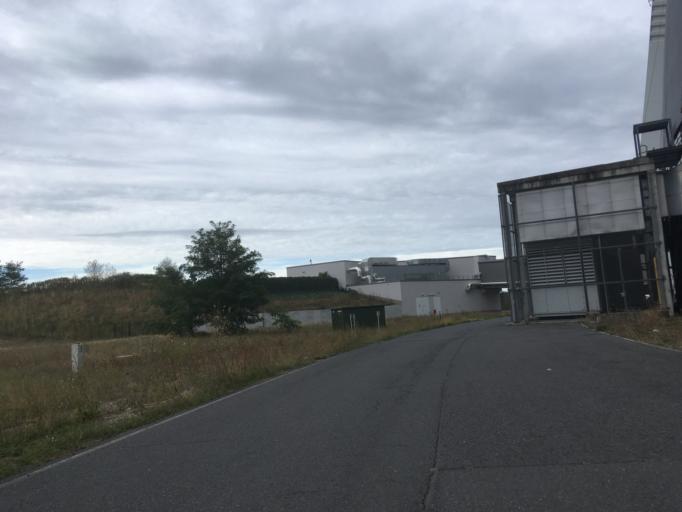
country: DE
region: Brandenburg
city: Halbe
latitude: 52.0388
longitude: 13.7510
